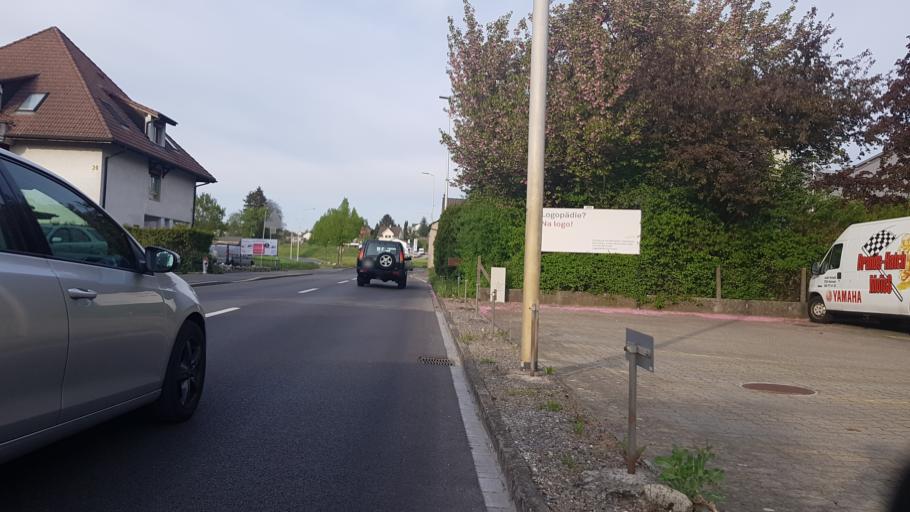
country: CH
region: Aargau
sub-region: Bezirk Kulm
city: Reinach
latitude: 47.2597
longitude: 8.1863
